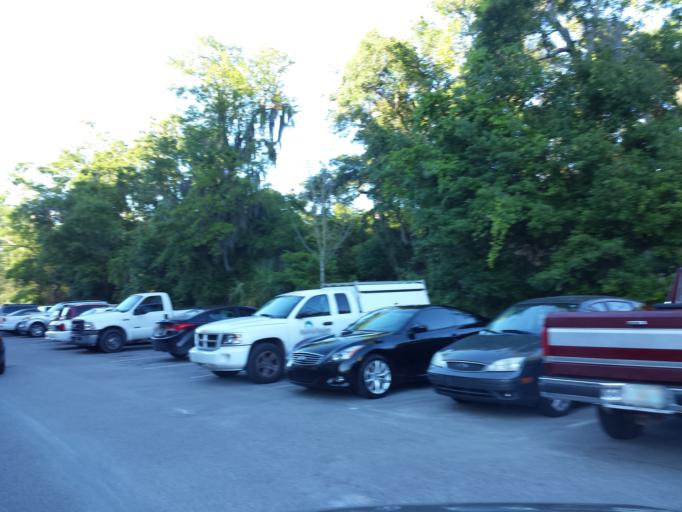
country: US
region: Florida
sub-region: Hillsborough County
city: Riverview
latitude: 27.8573
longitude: -82.3433
